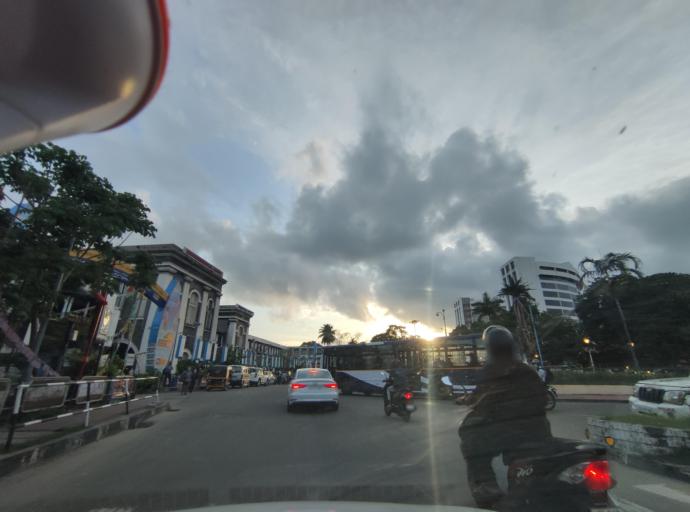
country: IN
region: Kerala
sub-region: Thiruvananthapuram
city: Thiruvananthapuram
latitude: 8.4881
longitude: 76.9507
